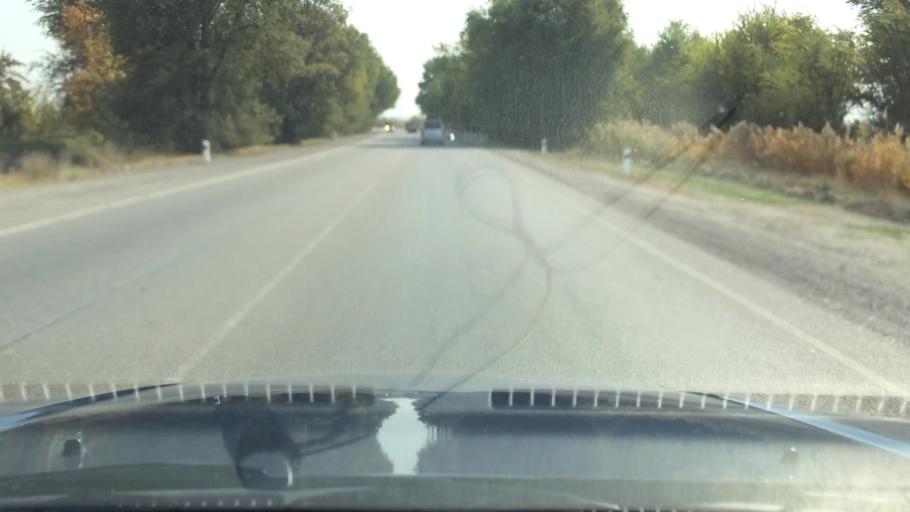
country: KG
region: Chuy
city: Lebedinovka
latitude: 42.9225
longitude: 74.7062
